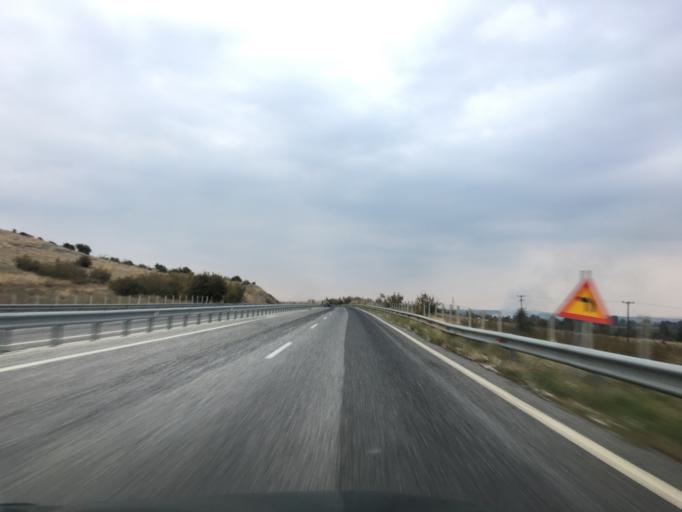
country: GR
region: Thessaly
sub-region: Trikala
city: Zarkos
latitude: 39.5981
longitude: 22.1988
